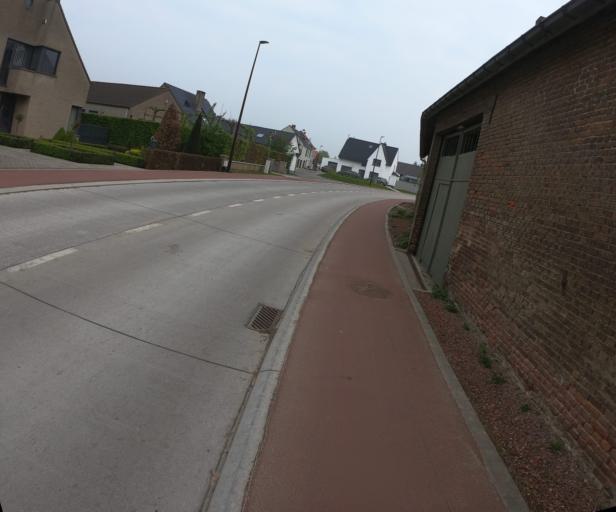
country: BE
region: Flanders
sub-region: Provincie Vlaams-Brabant
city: Lennik
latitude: 50.7911
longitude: 4.1528
